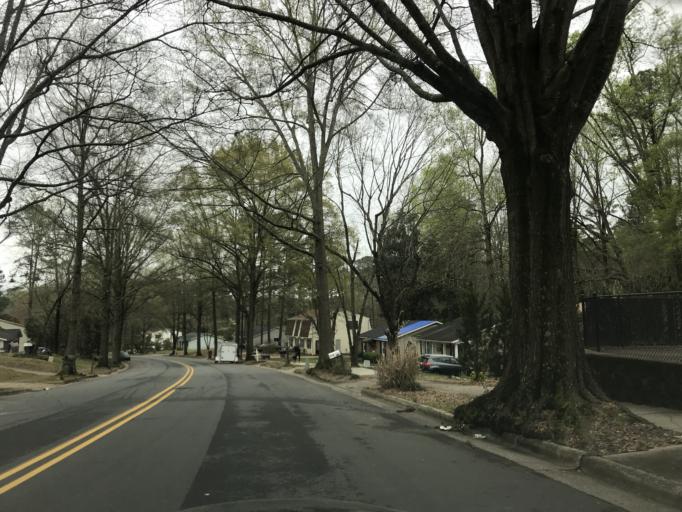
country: US
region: North Carolina
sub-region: Wake County
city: West Raleigh
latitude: 35.8761
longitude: -78.6502
